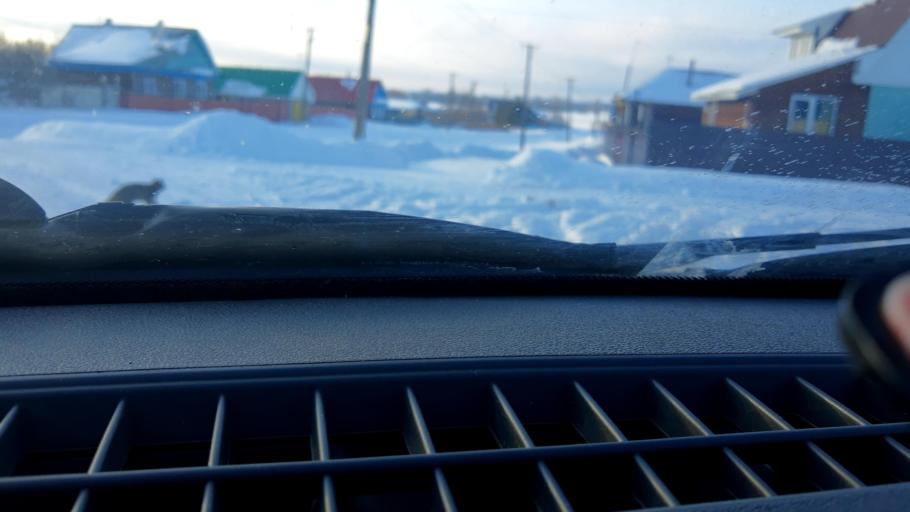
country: RU
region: Bashkortostan
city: Birsk
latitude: 55.1627
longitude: 55.6630
